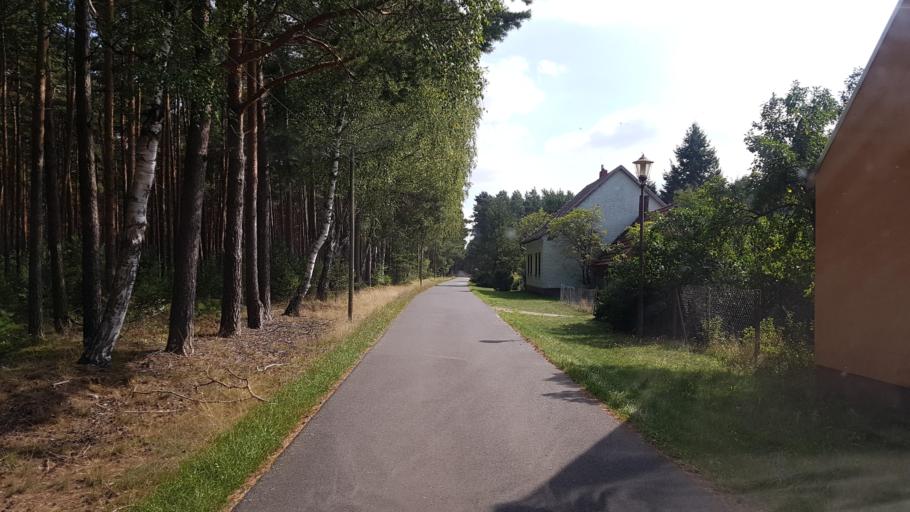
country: DE
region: Brandenburg
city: Hohenbucko
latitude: 51.7568
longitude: 13.5433
